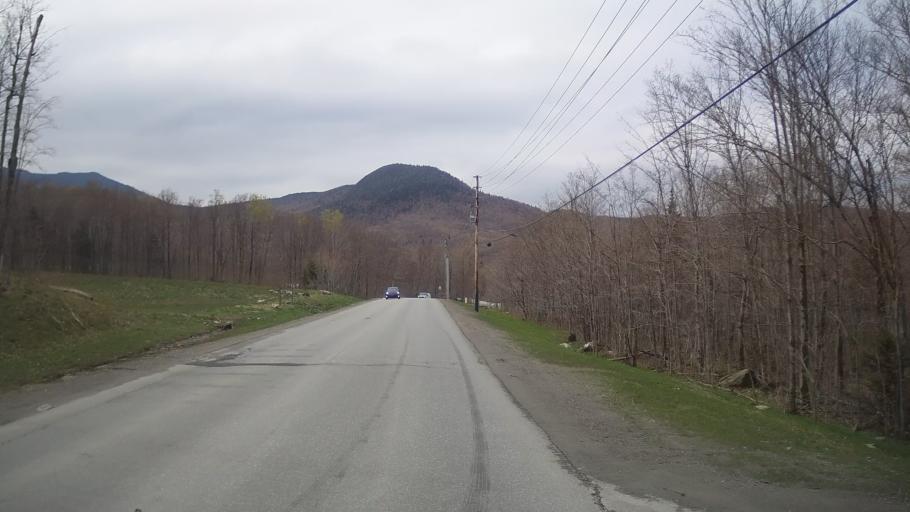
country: US
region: Vermont
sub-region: Franklin County
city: Richford
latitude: 44.9340
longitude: -72.4983
